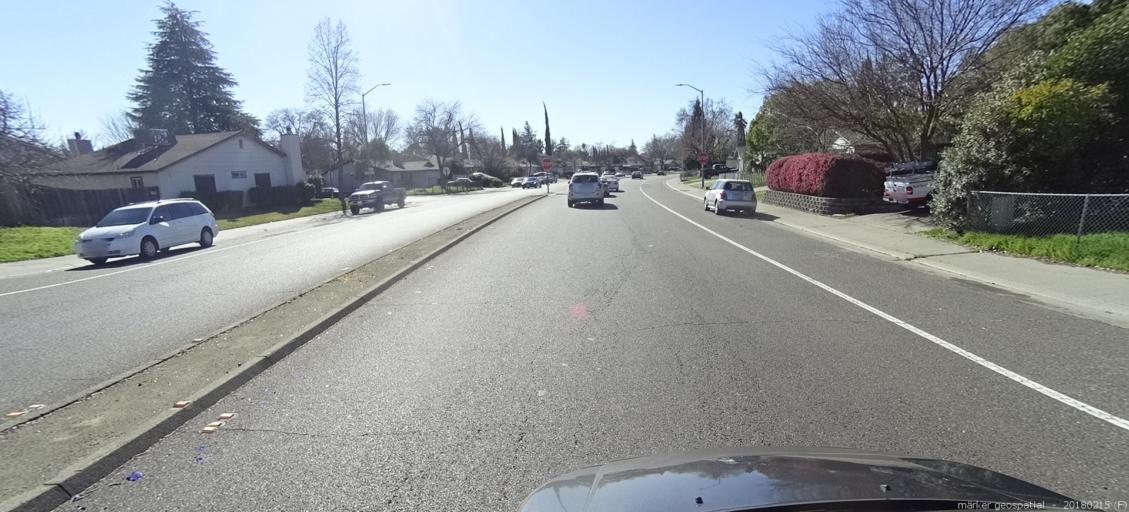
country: US
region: California
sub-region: Sacramento County
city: Foothill Farms
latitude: 38.6901
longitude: -121.3541
